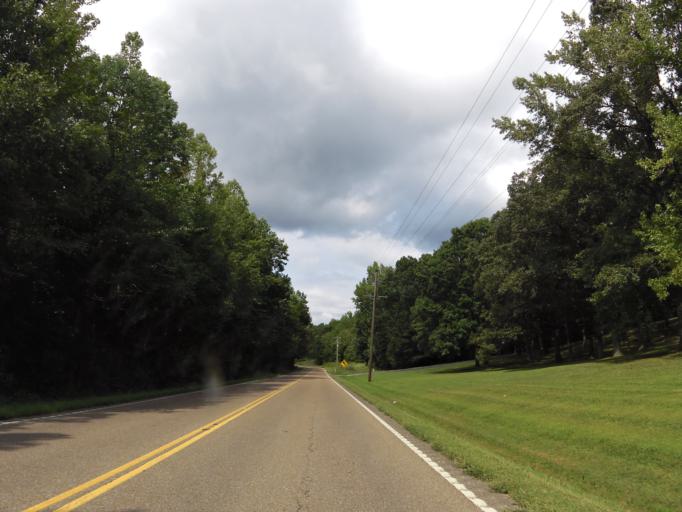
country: US
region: Tennessee
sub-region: Perry County
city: Linden
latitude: 35.6171
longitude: -87.8923
